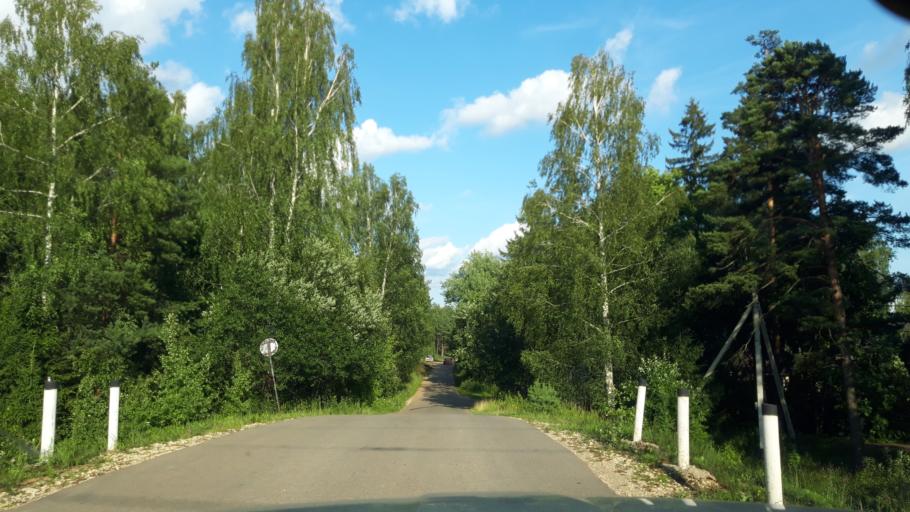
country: RU
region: Moskovskaya
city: Povarovo
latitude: 56.0620
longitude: 37.0850
